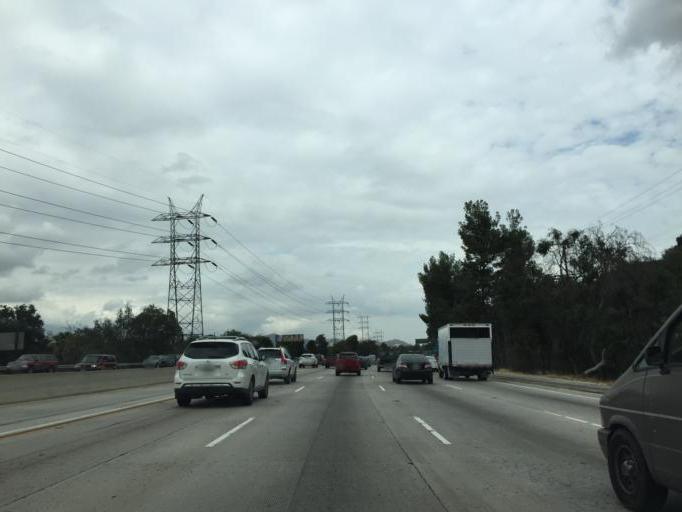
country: US
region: California
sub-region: Los Angeles County
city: Burbank
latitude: 34.1564
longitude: -118.3031
